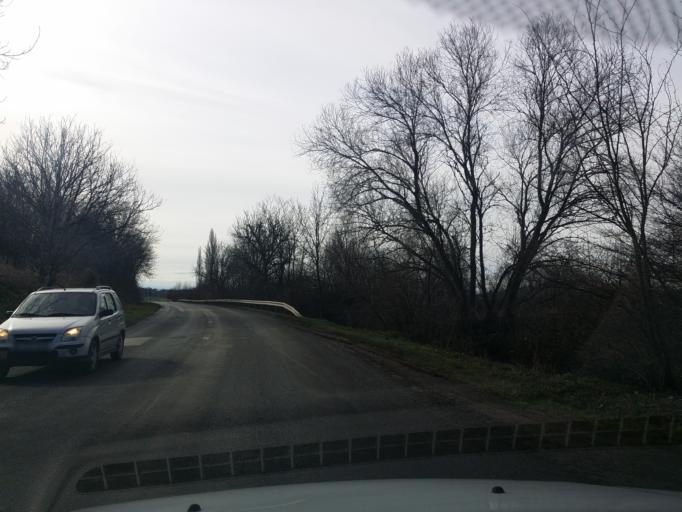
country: HU
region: Baranya
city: Villany
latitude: 45.9243
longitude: 18.4665
